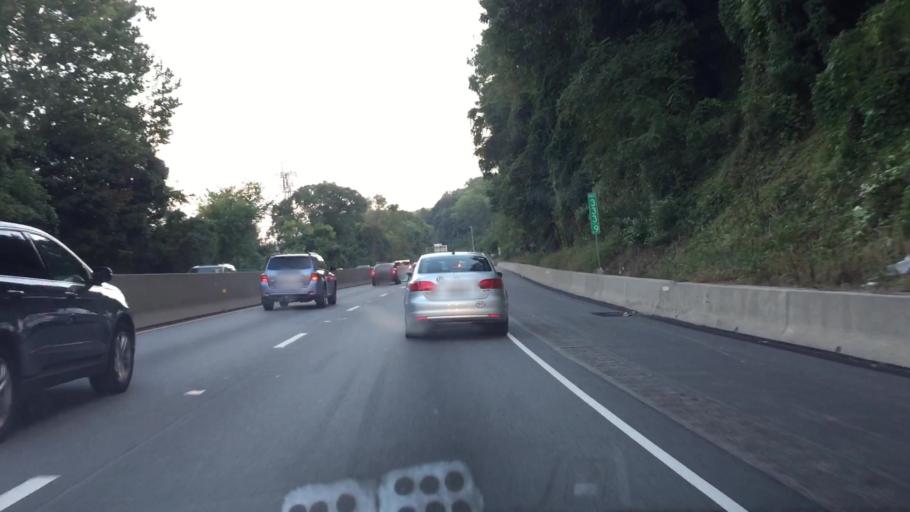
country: US
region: Pennsylvania
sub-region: Montgomery County
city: Conshohocken
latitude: 40.0689
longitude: -75.2795
